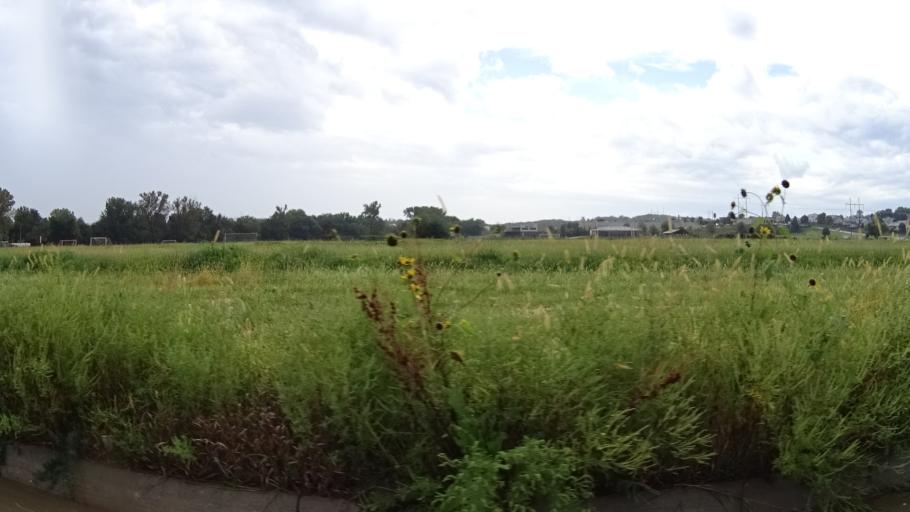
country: US
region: Nebraska
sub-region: Sarpy County
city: Offutt Air Force Base
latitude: 41.1451
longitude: -95.9731
